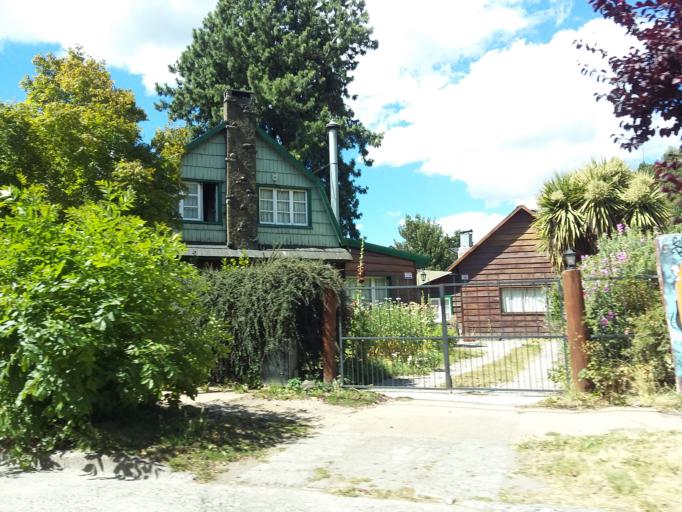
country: AR
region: Neuquen
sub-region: Departamento de Lacar
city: San Martin de los Andes
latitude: -40.1601
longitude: -71.3508
